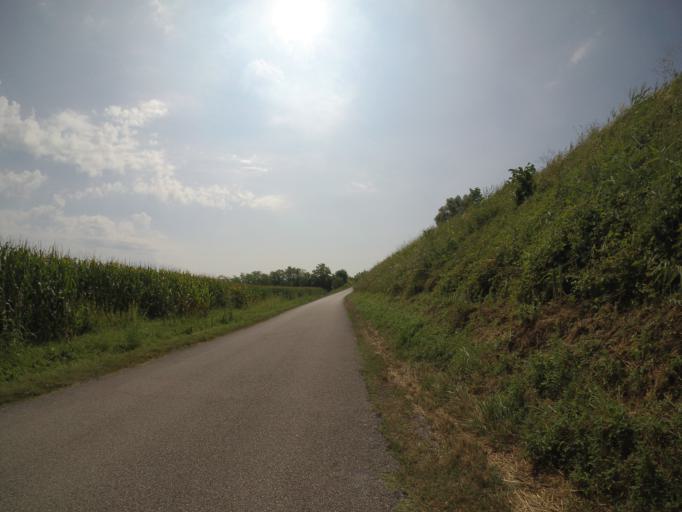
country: IT
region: Friuli Venezia Giulia
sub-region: Provincia di Udine
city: Pertegada
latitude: 45.7005
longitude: 13.0520
